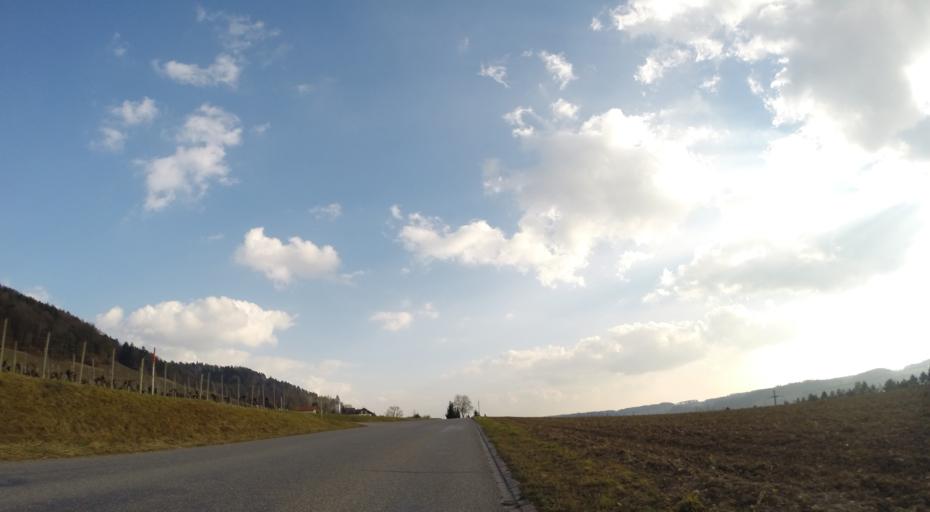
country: CH
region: Thurgau
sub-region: Frauenfeld District
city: Diessenhofen
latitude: 47.6465
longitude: 8.7877
